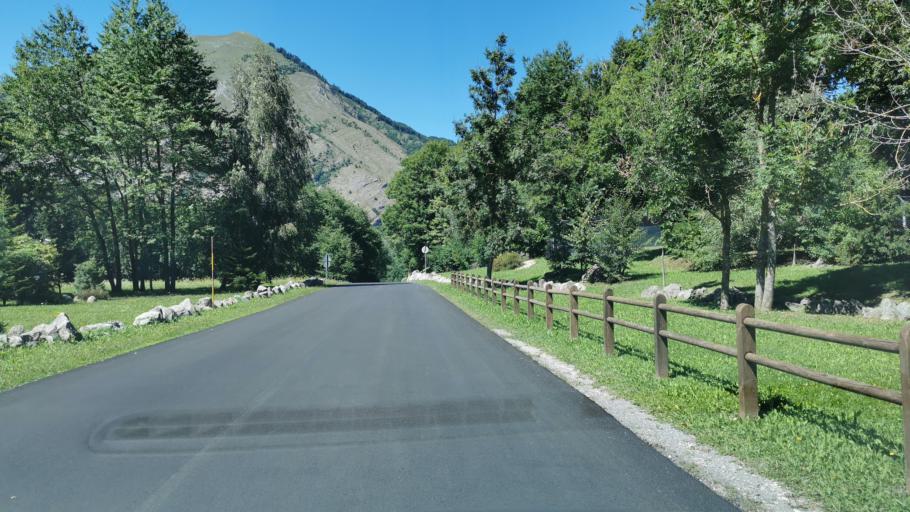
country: IT
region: Piedmont
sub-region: Provincia di Cuneo
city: Entracque
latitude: 44.2505
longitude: 7.3843
